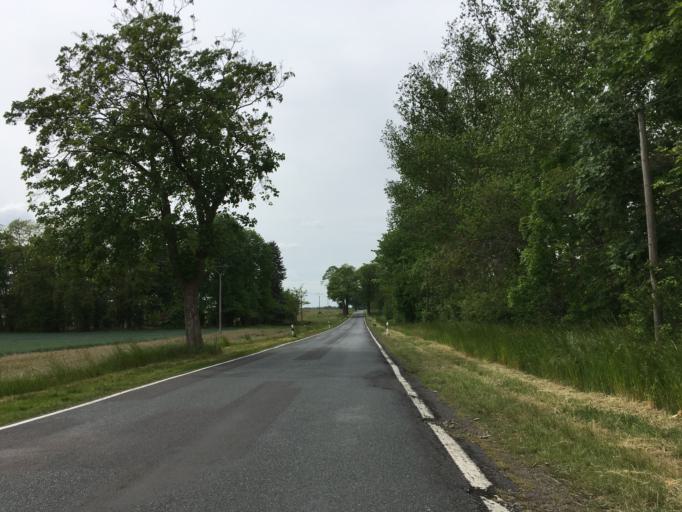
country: DE
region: Brandenburg
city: Werftpfuhl
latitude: 52.7309
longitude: 13.7821
